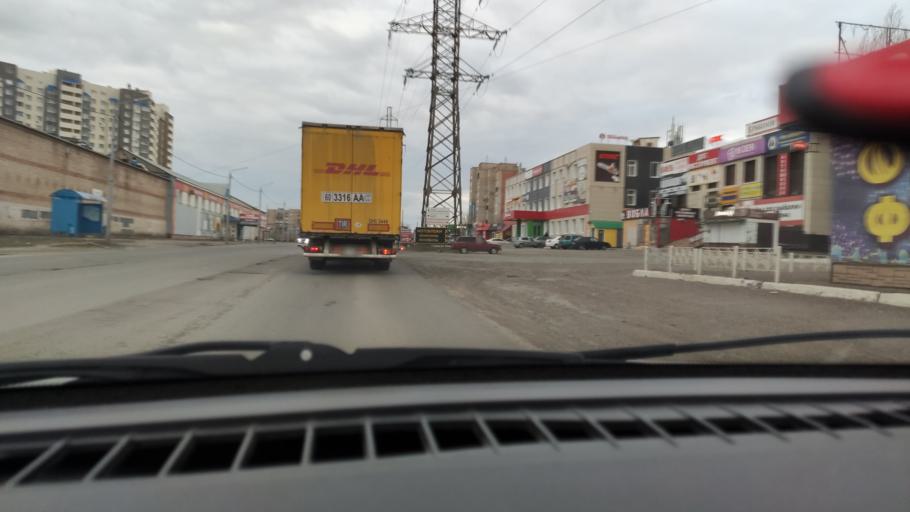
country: RU
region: Orenburg
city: Orenburg
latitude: 51.7859
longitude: 55.1732
